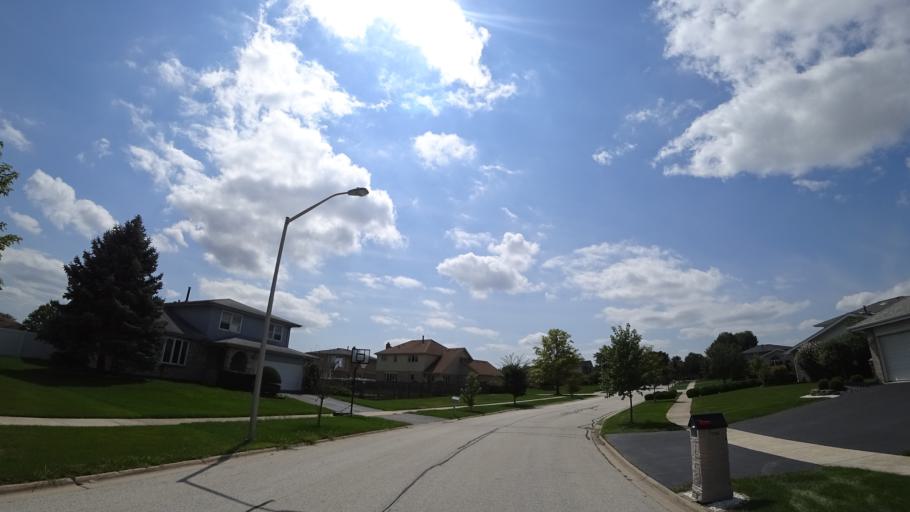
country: US
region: Illinois
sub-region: Cook County
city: Orland Hills
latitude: 41.5674
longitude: -87.8475
